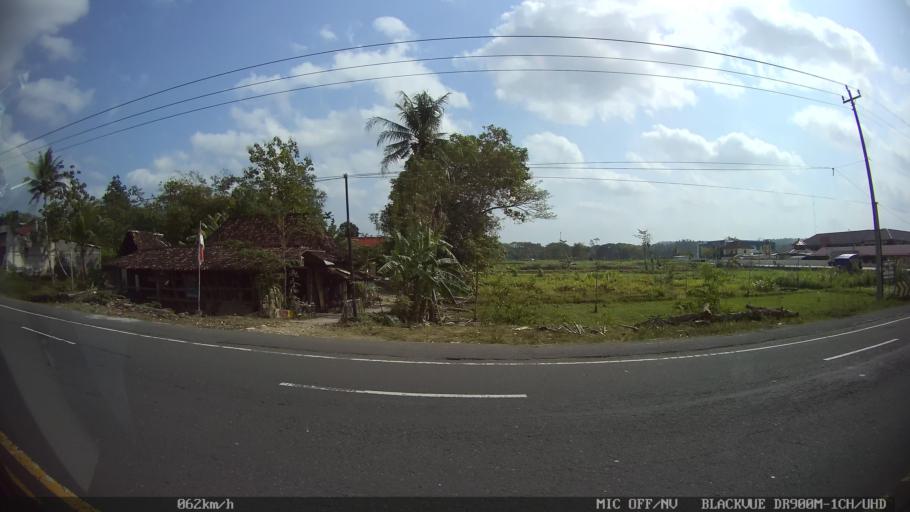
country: ID
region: Daerah Istimewa Yogyakarta
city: Srandakan
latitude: -7.8669
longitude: 110.1745
